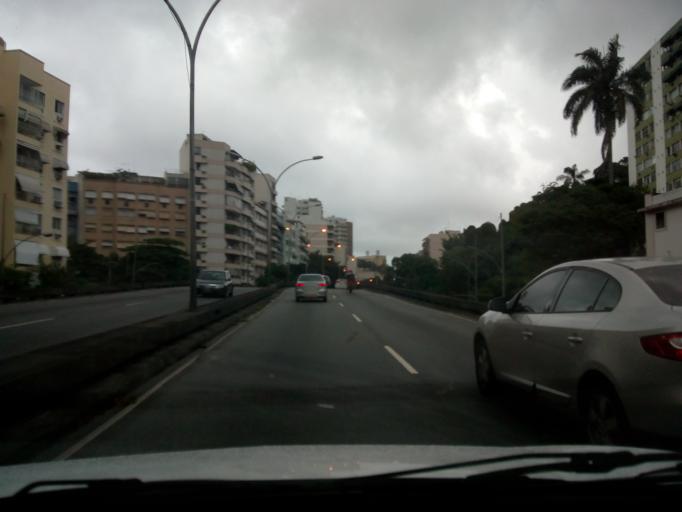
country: BR
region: Rio de Janeiro
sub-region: Rio De Janeiro
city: Rio de Janeiro
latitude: -22.9325
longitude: -43.1851
